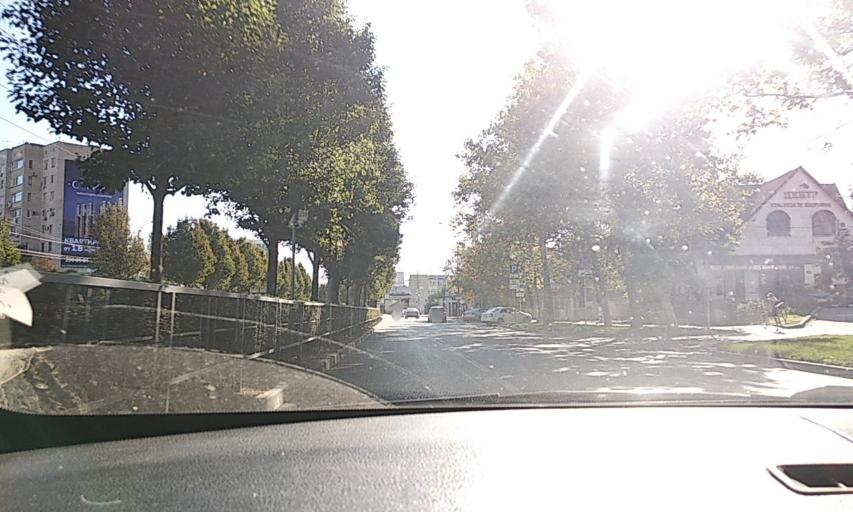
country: RU
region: Krasnodarskiy
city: Pashkovskiy
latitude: 45.0130
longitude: 39.0518
